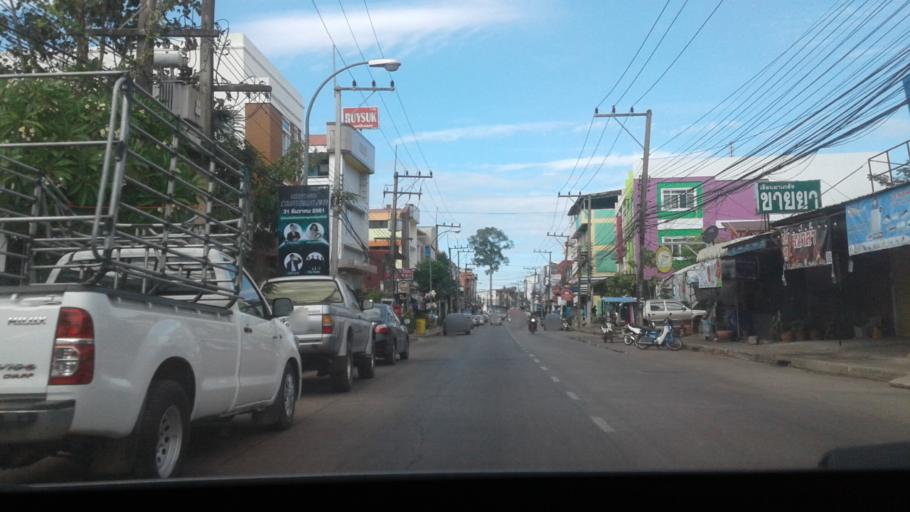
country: TH
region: Changwat Udon Thani
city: Udon Thani
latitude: 17.4142
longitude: 102.8001
